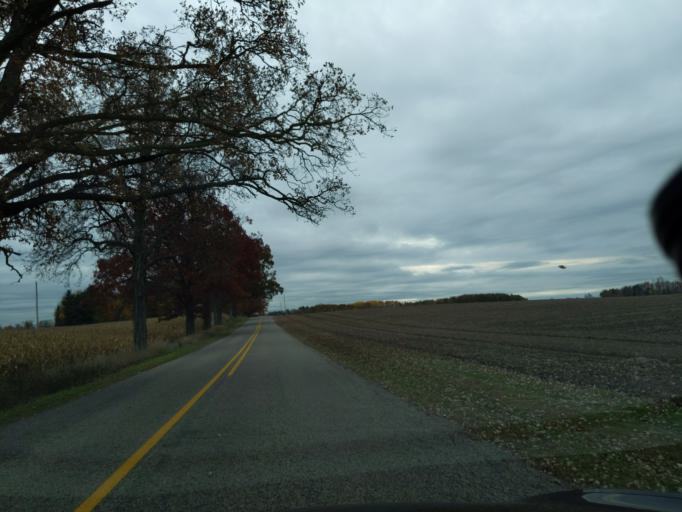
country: US
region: Michigan
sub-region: Eaton County
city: Eaton Rapids
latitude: 42.5058
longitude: -84.6013
